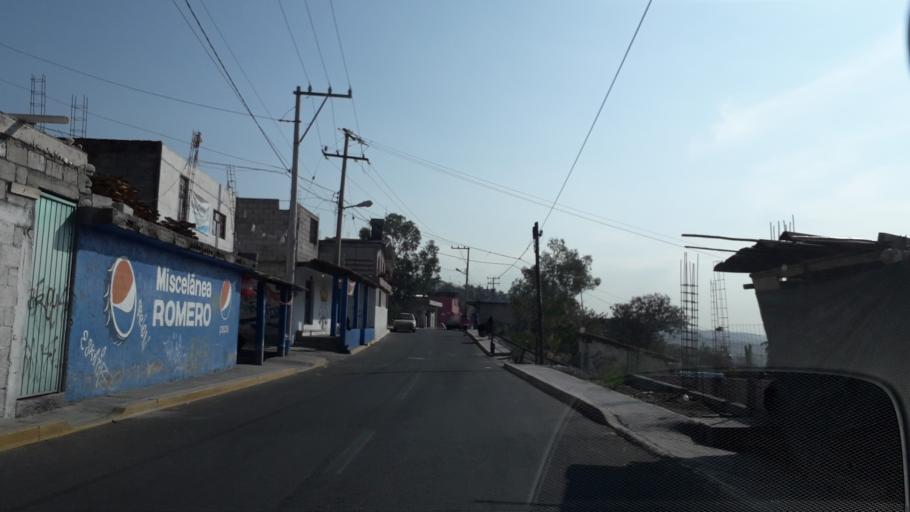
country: MX
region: Puebla
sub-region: Puebla
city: San Andres Azumiatla
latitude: 18.9027
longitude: -98.2560
